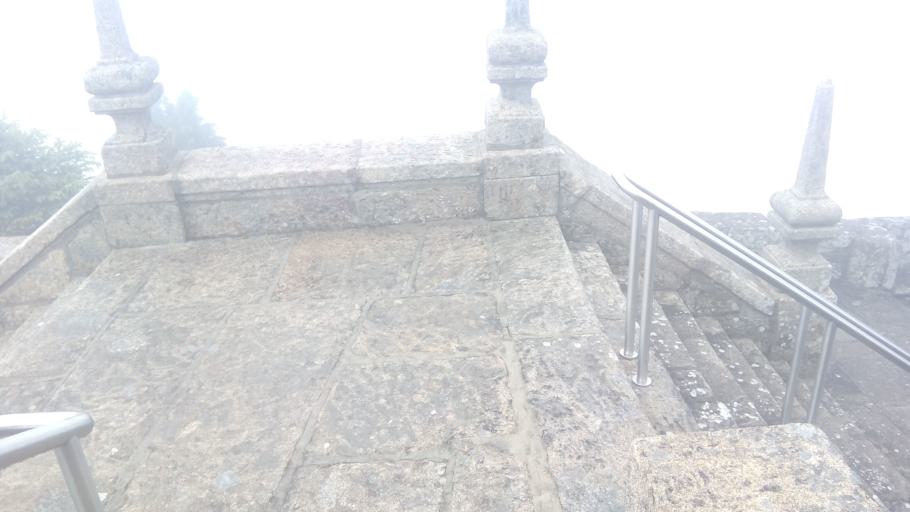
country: PT
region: Vila Real
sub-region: Mondim de Basto
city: Mondim de Basto
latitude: 41.4164
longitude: -7.9160
